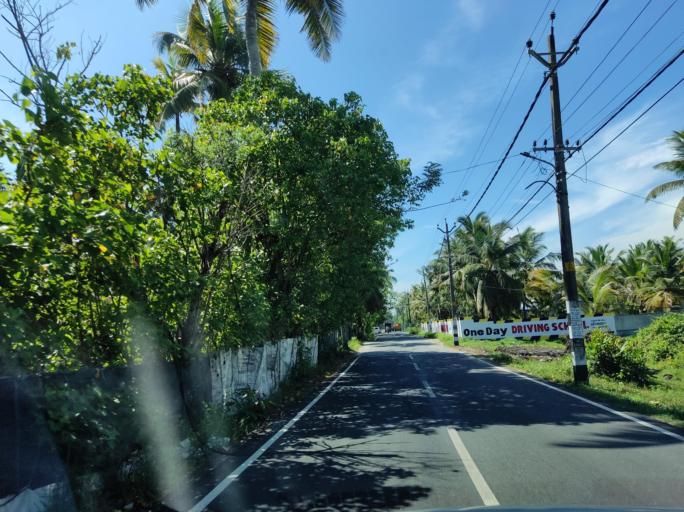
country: IN
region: Kerala
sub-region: Alappuzha
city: Kayankulam
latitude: 9.1718
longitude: 76.4475
